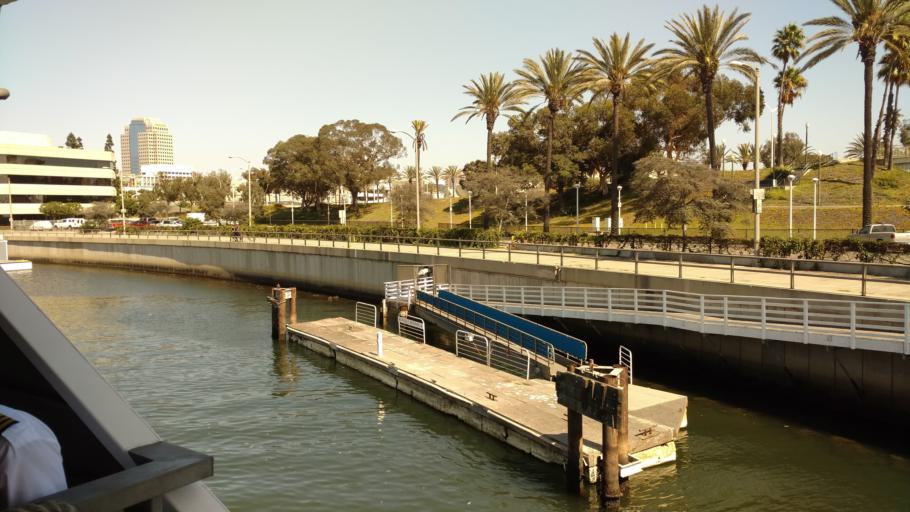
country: US
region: California
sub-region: Los Angeles County
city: Long Beach
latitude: 33.7616
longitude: -118.1995
